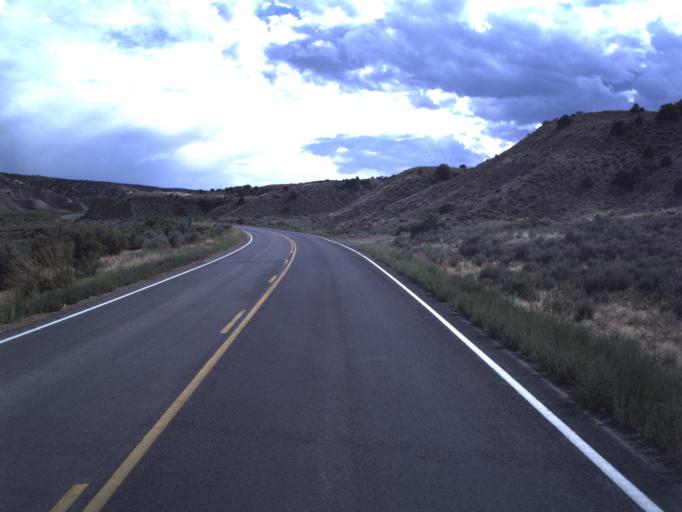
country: US
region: Utah
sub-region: Duchesne County
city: Duchesne
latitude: 40.1430
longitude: -110.4217
